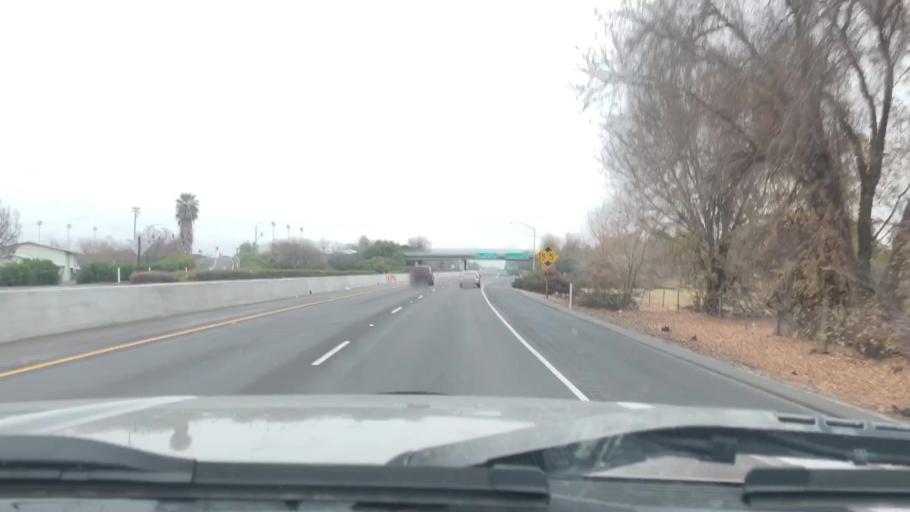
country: US
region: California
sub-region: Kings County
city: Lemoore
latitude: 36.2916
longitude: -119.7835
